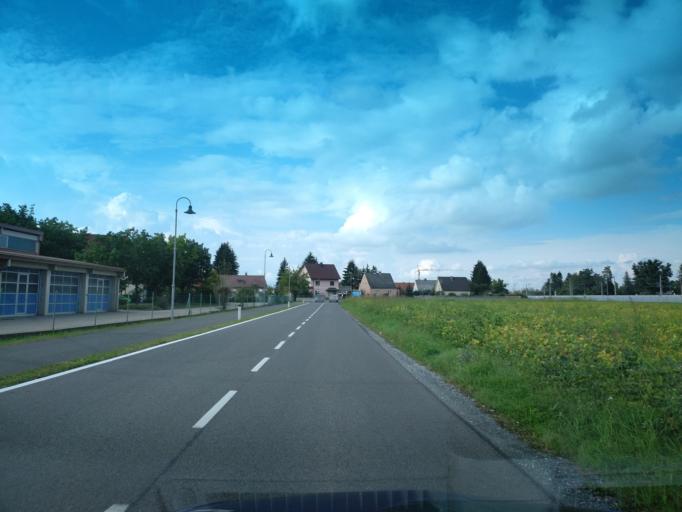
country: AT
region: Styria
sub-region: Politischer Bezirk Leibnitz
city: Leibnitz
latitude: 46.7842
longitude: 15.5450
